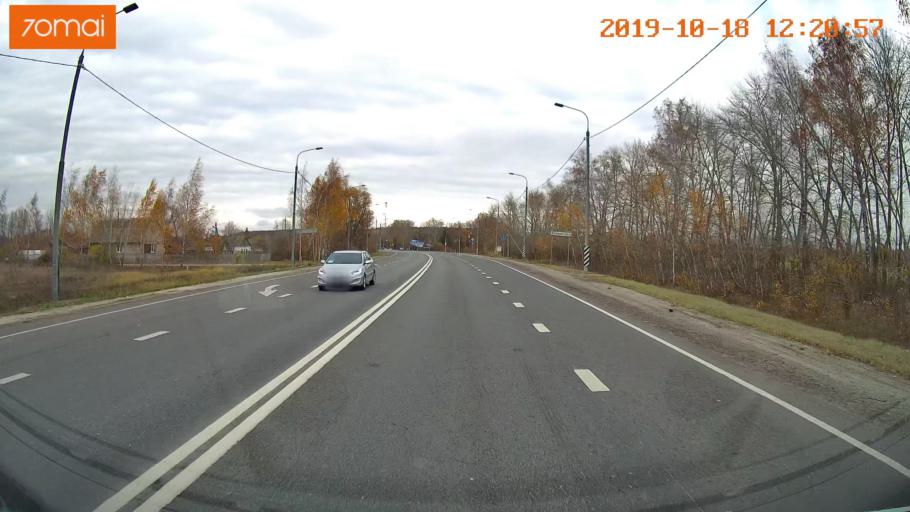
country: RU
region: Rjazan
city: Bagramovo
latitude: 54.5053
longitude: 39.4861
